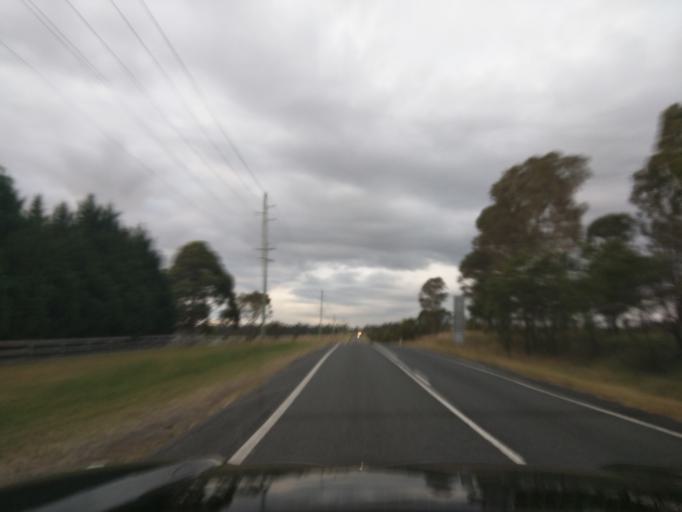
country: AU
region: New South Wales
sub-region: Wollondilly
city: Douglas Park
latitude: -34.2168
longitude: 150.7729
